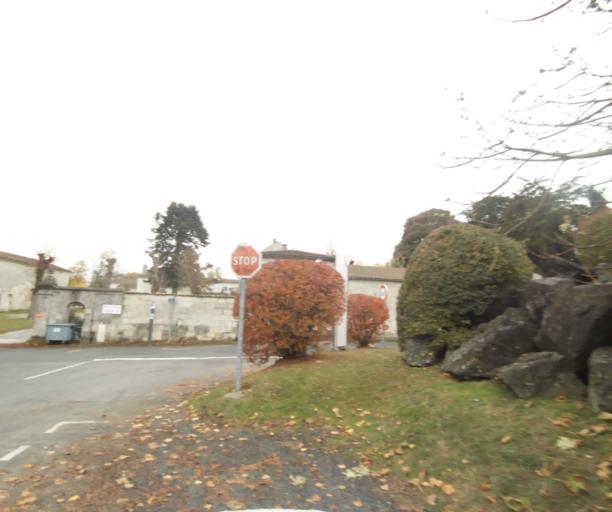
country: FR
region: Poitou-Charentes
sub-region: Departement de la Charente-Maritime
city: Saintes
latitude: 45.7397
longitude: -0.6642
